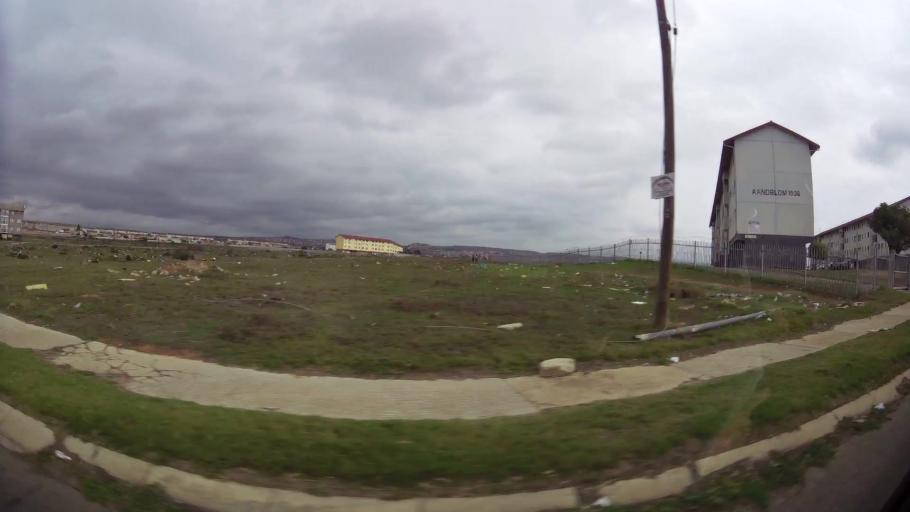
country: ZA
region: Eastern Cape
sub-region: Nelson Mandela Bay Metropolitan Municipality
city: Port Elizabeth
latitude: -33.8891
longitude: 25.5620
